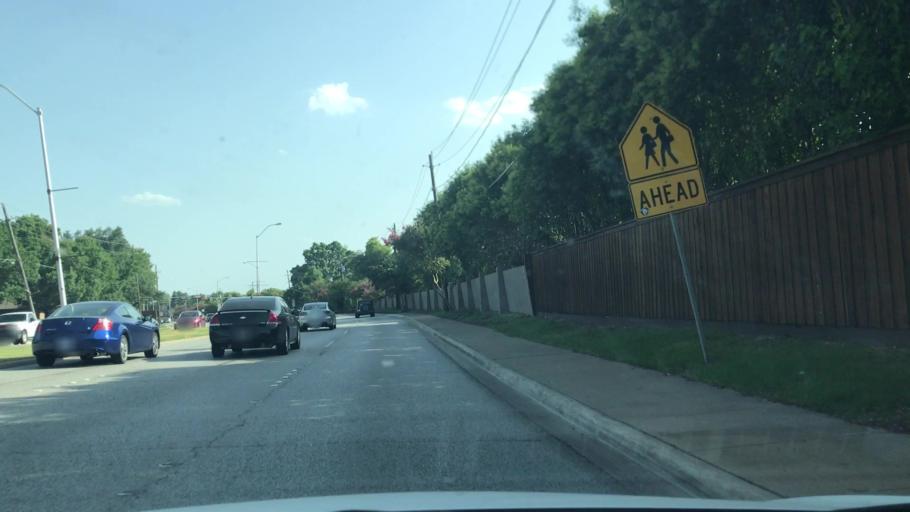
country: US
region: Texas
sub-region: Dallas County
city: Richardson
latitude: 32.9759
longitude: -96.7685
